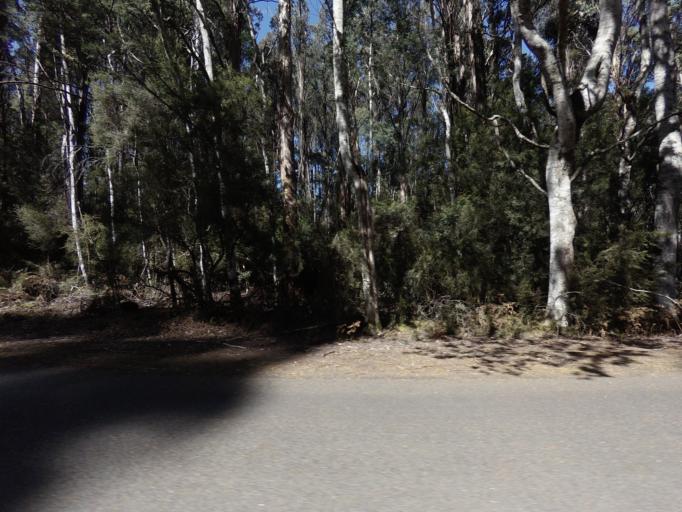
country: AU
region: Tasmania
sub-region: Derwent Valley
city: New Norfolk
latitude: -42.7670
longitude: 146.5892
